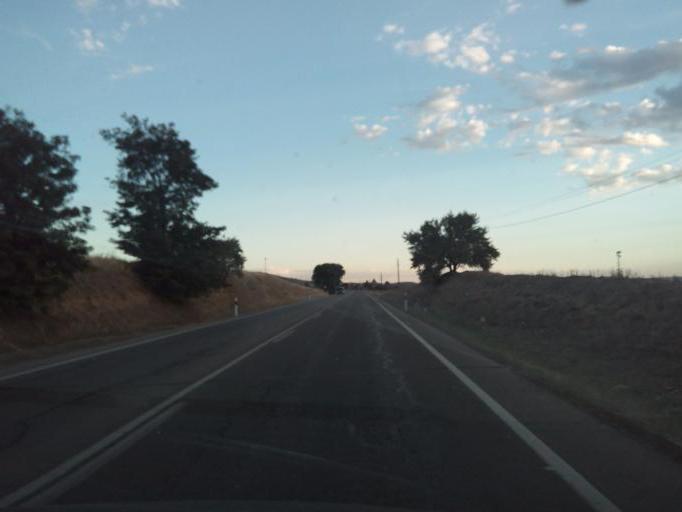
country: ES
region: Madrid
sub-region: Provincia de Madrid
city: Algete
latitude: 40.5910
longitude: -3.5072
